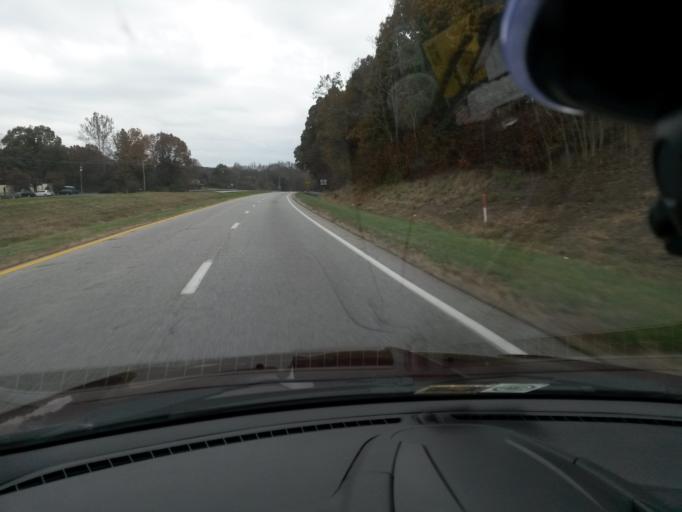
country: US
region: Virginia
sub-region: Amherst County
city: Amherst
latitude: 37.6646
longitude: -78.9543
